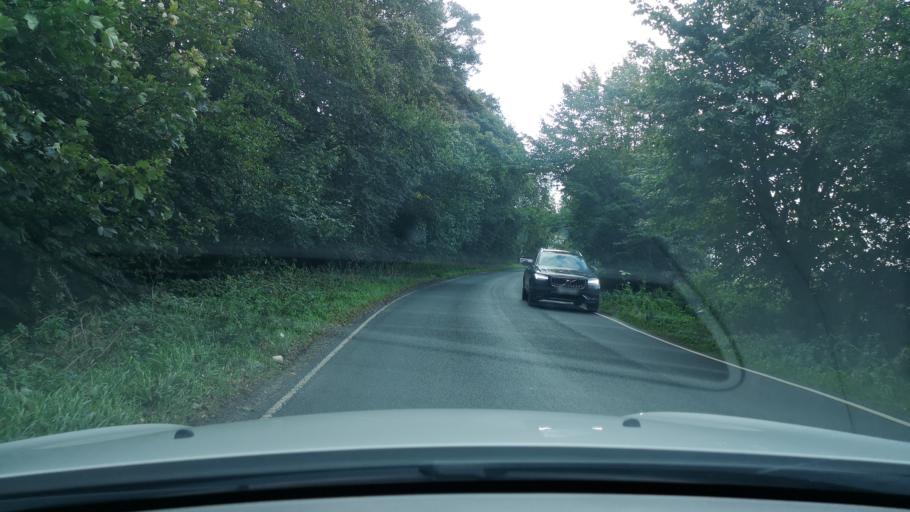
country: GB
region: England
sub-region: East Riding of Yorkshire
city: Walkington
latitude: 53.8337
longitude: -0.4883
